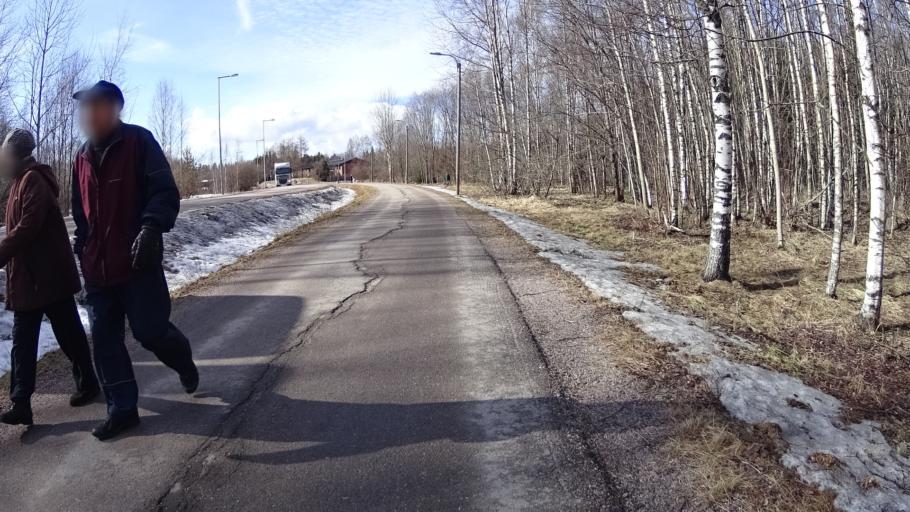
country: FI
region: Uusimaa
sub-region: Helsinki
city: Kilo
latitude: 60.2689
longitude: 24.8286
